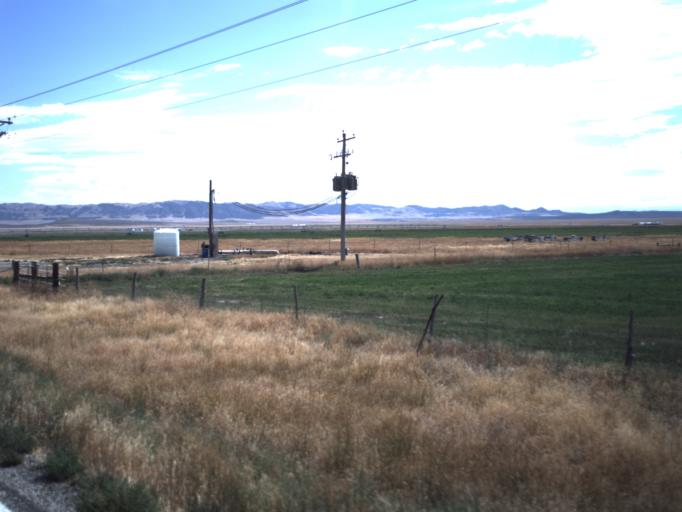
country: US
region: Idaho
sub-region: Oneida County
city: Malad City
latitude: 41.9668
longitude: -112.8833
